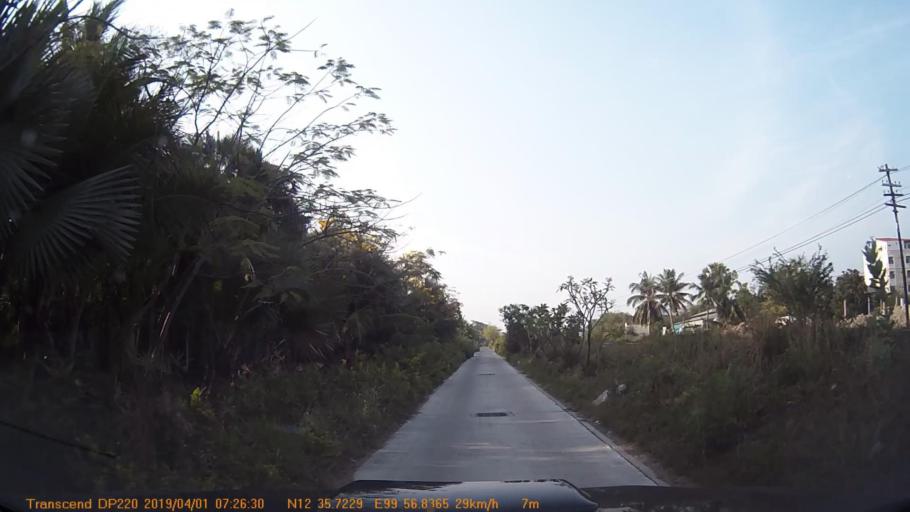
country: TH
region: Prachuap Khiri Khan
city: Hua Hin
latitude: 12.5952
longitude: 99.9473
